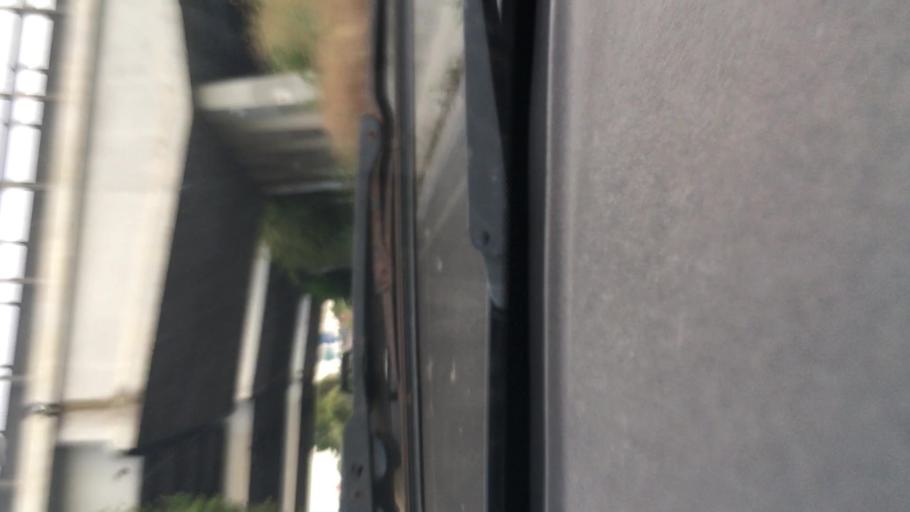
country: IT
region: Latium
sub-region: Citta metropolitana di Roma Capitale
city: Vitinia
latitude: 41.8080
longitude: 12.4204
